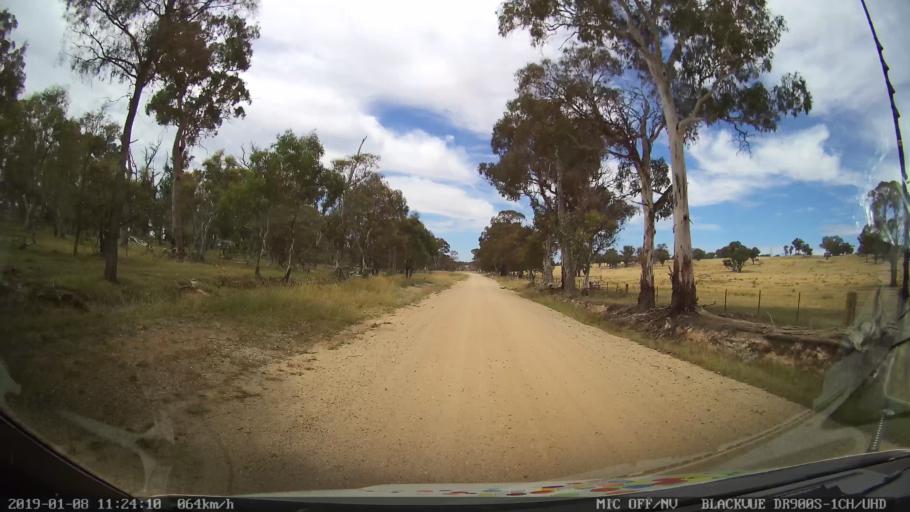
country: AU
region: New South Wales
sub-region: Guyra
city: Guyra
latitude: -30.2621
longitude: 151.5583
